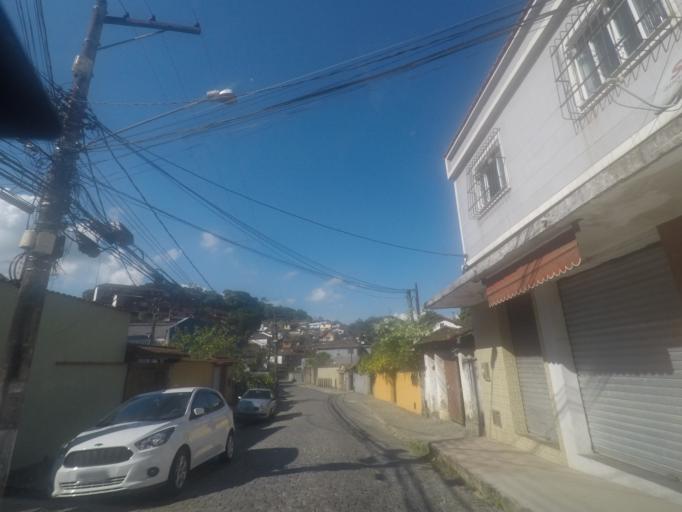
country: BR
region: Rio de Janeiro
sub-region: Petropolis
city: Petropolis
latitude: -22.5379
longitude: -43.1998
